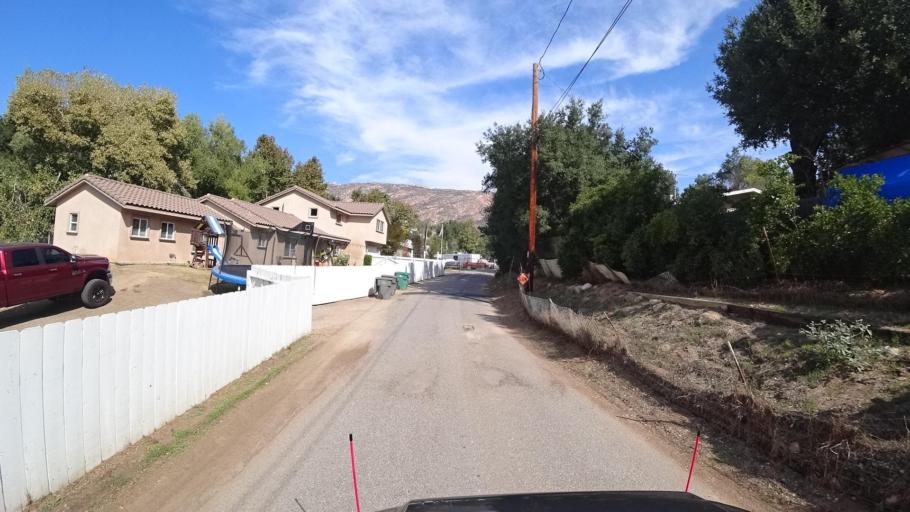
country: US
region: California
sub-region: San Diego County
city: Harbison Canyon
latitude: 32.8166
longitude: -116.8332
